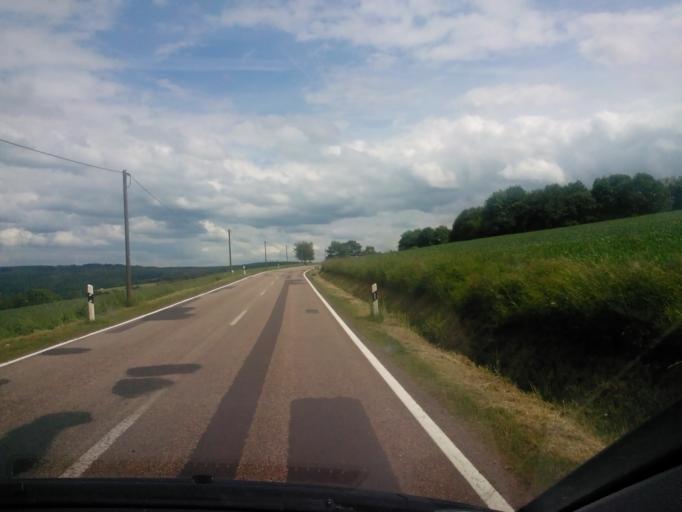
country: DE
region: Saarland
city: Eppelborn
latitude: 49.4315
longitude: 7.0057
